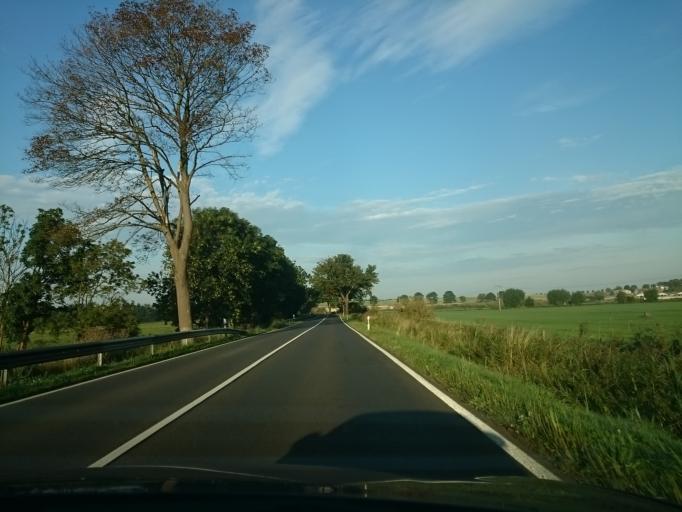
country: DE
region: Mecklenburg-Vorpommern
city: Wolgast
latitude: 54.0419
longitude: 13.7296
